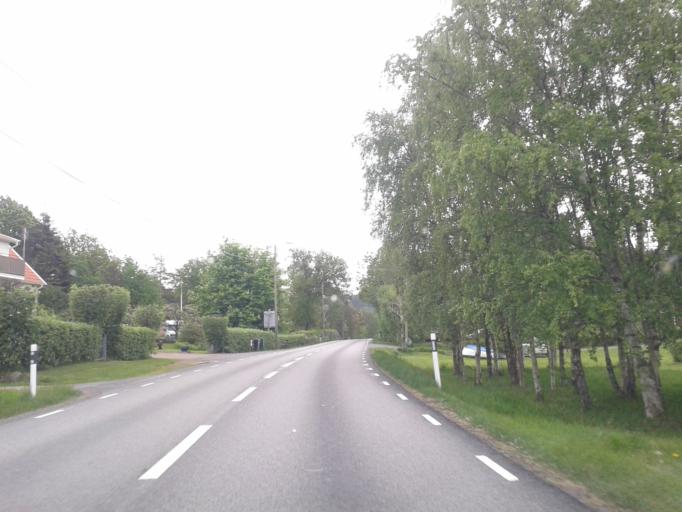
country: SE
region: Vaestra Goetaland
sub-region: Kungalvs Kommun
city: Kode
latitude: 57.8943
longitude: 11.7409
